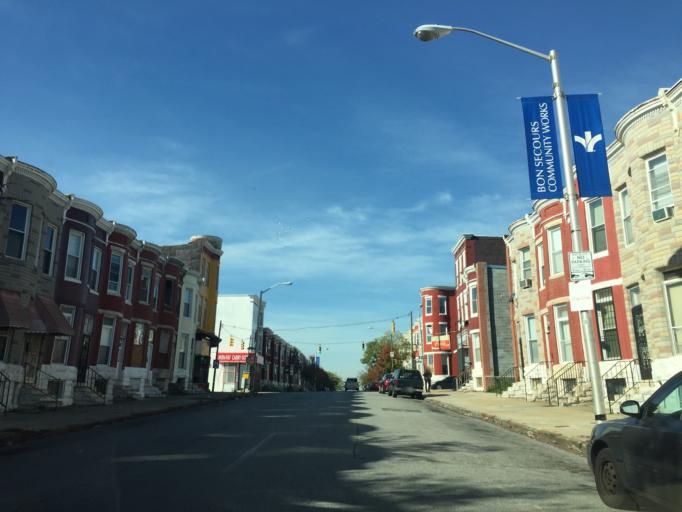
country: US
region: Maryland
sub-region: City of Baltimore
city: Baltimore
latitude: 39.2895
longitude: -76.6462
